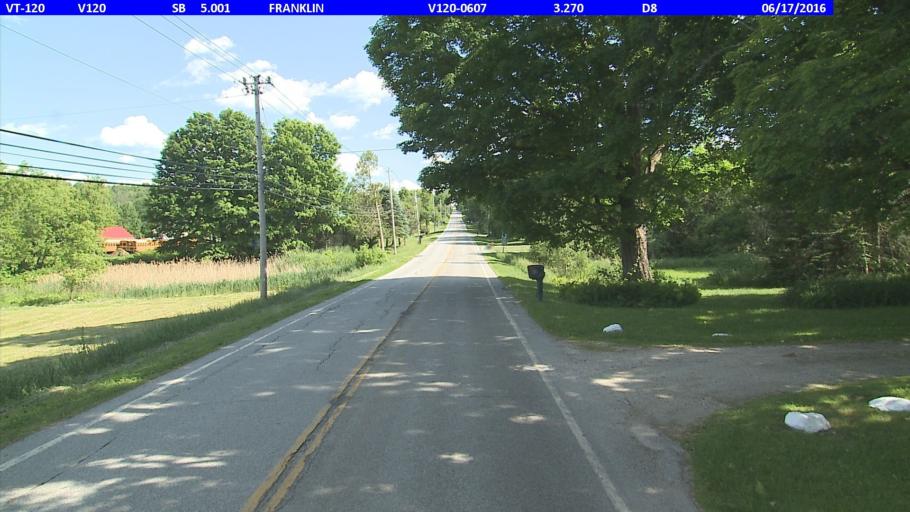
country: US
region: Vermont
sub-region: Franklin County
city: Enosburg Falls
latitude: 44.9792
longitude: -72.9144
